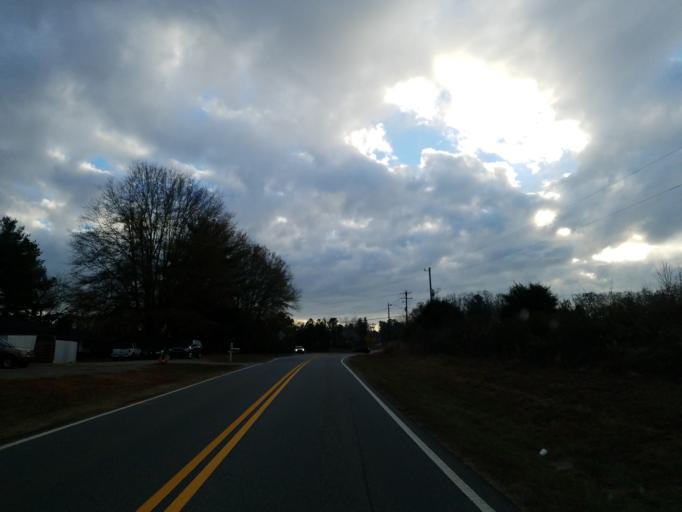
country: US
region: Georgia
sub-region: Dawson County
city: Dawsonville
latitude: 34.3248
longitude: -84.0725
